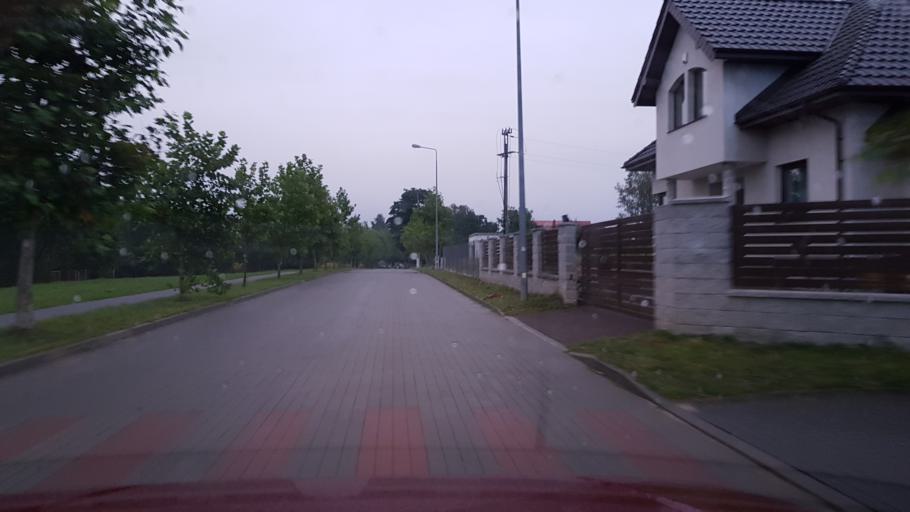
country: PL
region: West Pomeranian Voivodeship
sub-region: Powiat slawienski
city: Slawno
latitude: 54.3477
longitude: 16.6697
